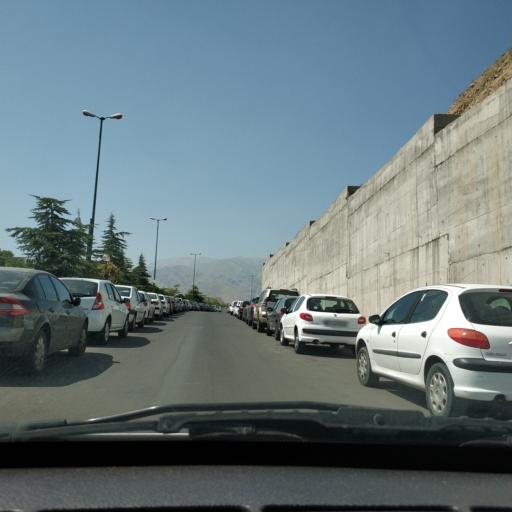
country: IR
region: Tehran
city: Tajrish
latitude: 35.7511
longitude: 51.4356
